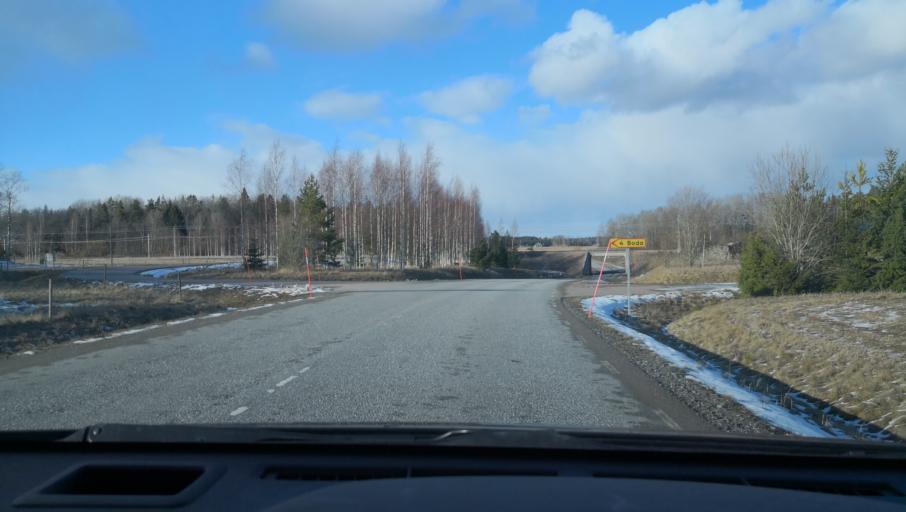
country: SE
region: Uppsala
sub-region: Enkopings Kommun
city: Hummelsta
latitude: 59.6498
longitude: 16.9643
